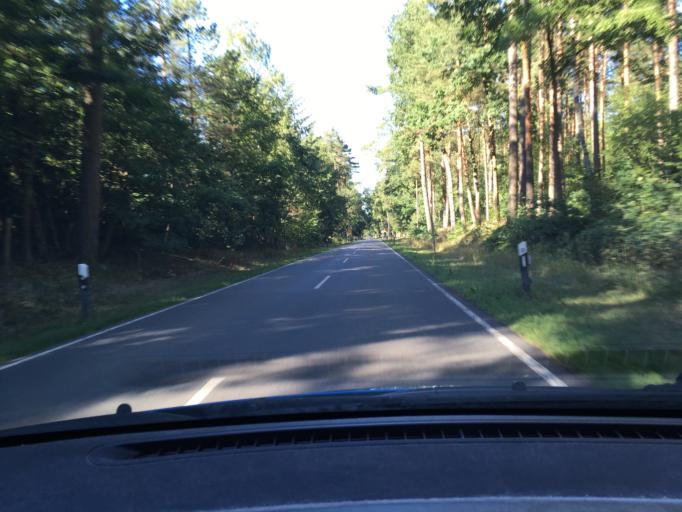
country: DE
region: Lower Saxony
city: Neetze
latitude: 53.2867
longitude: 10.6470
